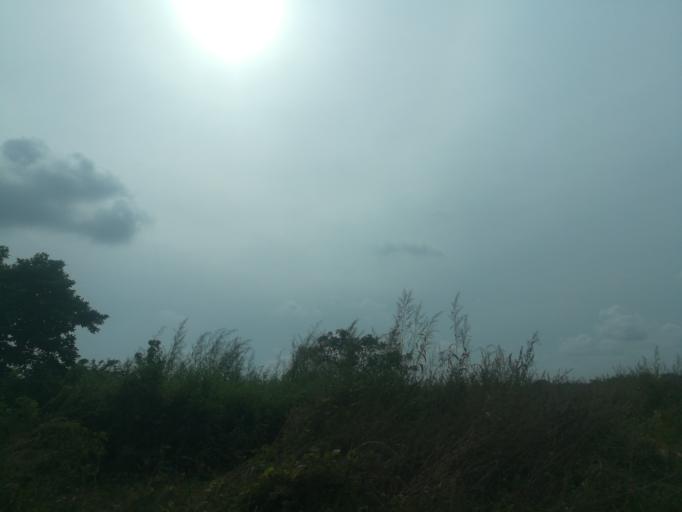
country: NG
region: Ogun
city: Ayetoro
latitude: 7.2963
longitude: 3.0776
